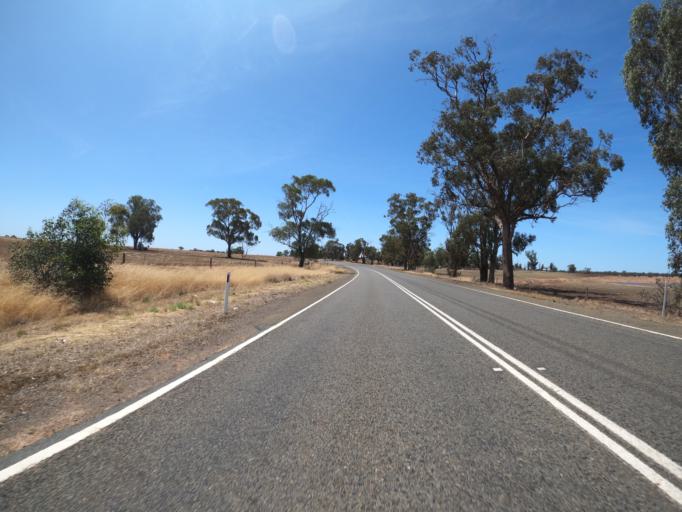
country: AU
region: Victoria
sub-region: Moira
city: Yarrawonga
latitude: -36.1001
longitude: 145.9942
